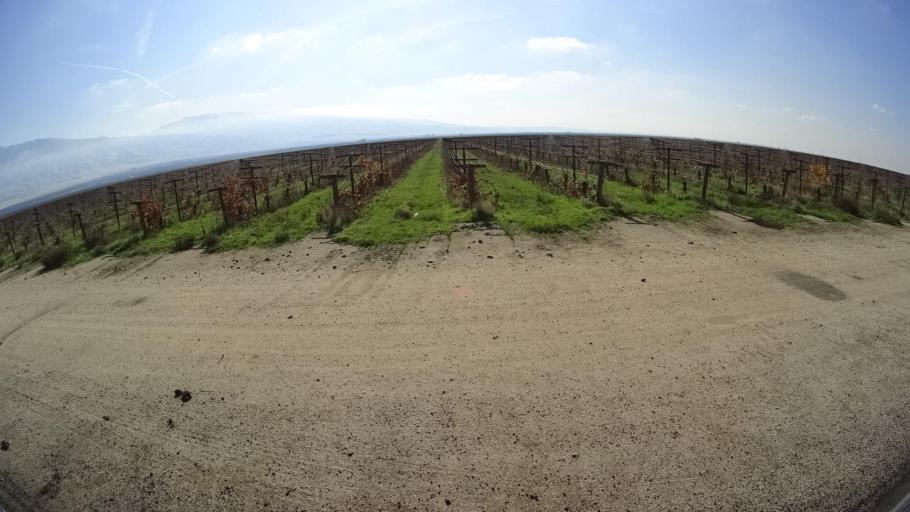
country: US
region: California
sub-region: Kern County
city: Arvin
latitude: 35.2675
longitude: -118.7819
